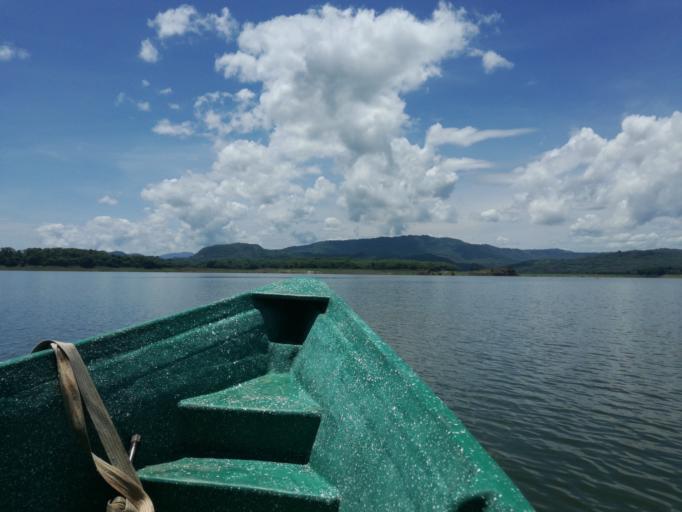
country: SV
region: Cuscatlan
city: Suchitoto
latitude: 13.9442
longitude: -89.0055
